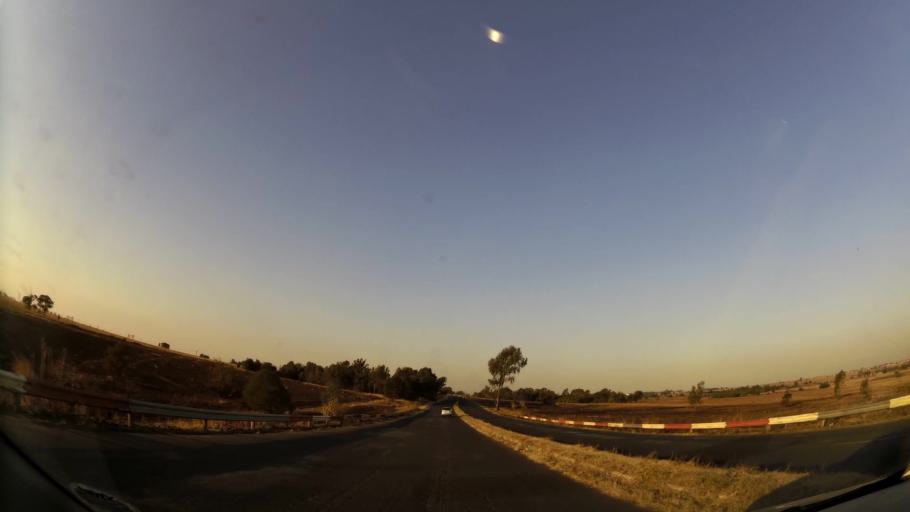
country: ZA
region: Gauteng
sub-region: West Rand District Municipality
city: Randfontein
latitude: -26.2045
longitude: 27.6650
